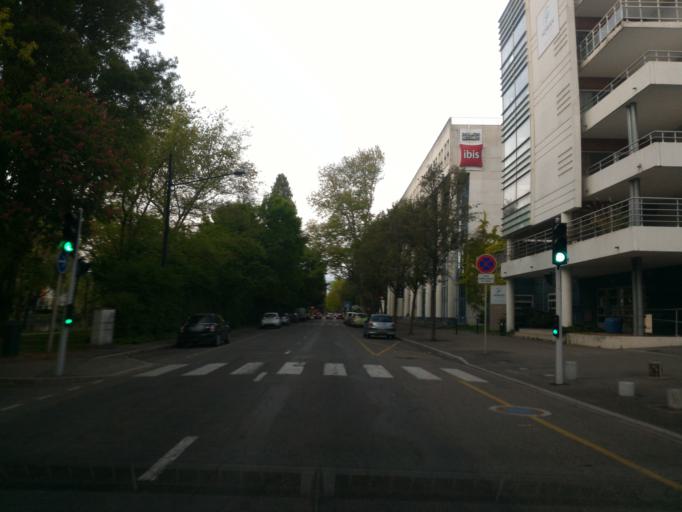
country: FR
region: Alsace
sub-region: Departement du Haut-Rhin
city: Mulhouse
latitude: 47.7544
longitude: 7.3491
